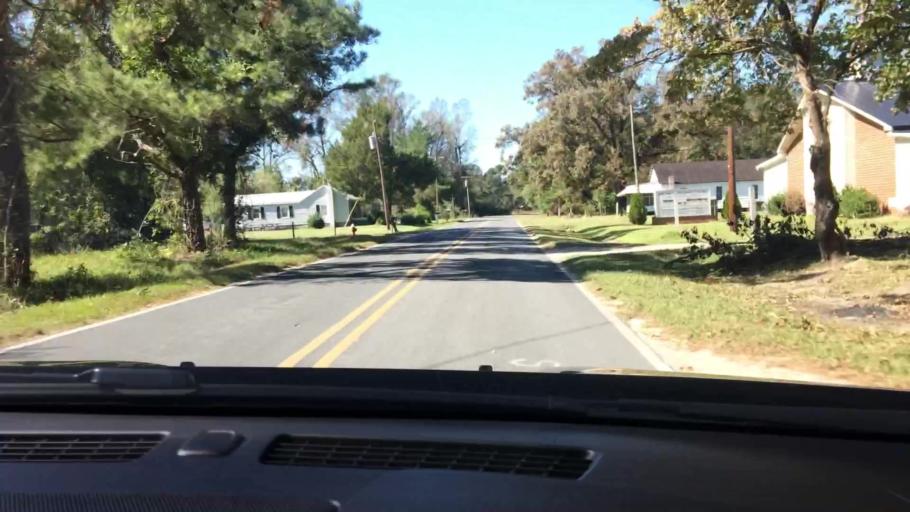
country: US
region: North Carolina
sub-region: Pitt County
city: Grifton
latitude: 35.2924
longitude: -77.3295
